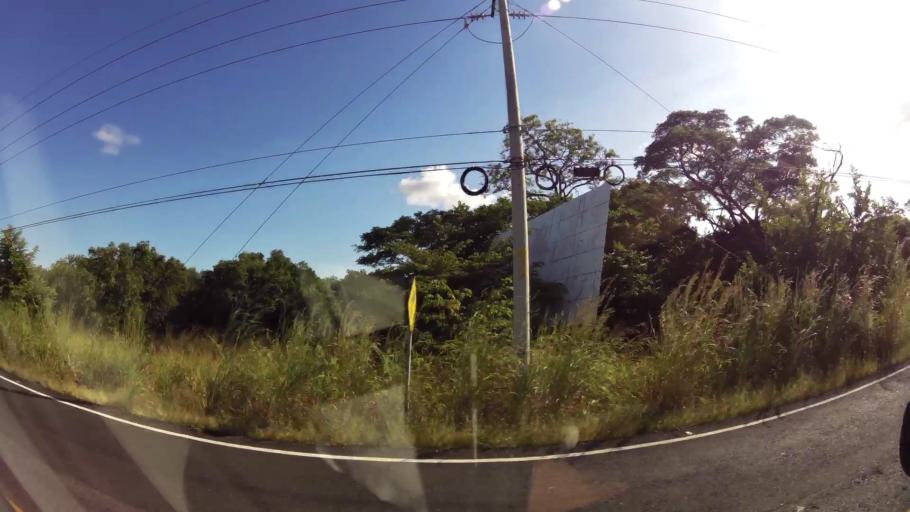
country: CR
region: Guanacaste
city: Sardinal
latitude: 10.5665
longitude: -85.5996
